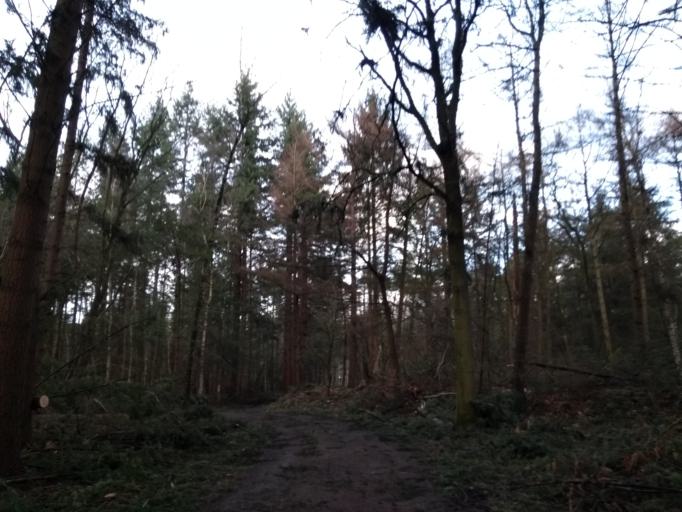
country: NL
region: Overijssel
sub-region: Gemeente Enschede
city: Enschede
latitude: 52.2591
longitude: 6.8738
